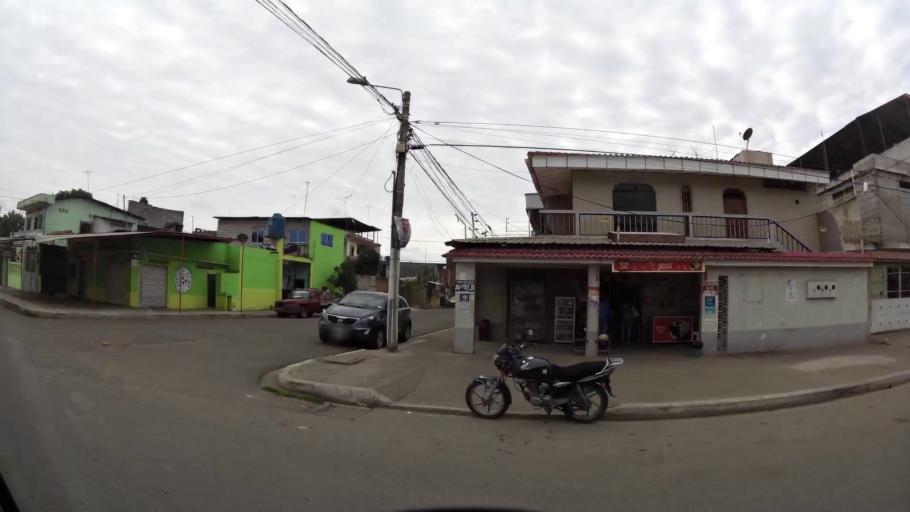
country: EC
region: El Oro
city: Machala
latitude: -3.2475
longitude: -79.9509
